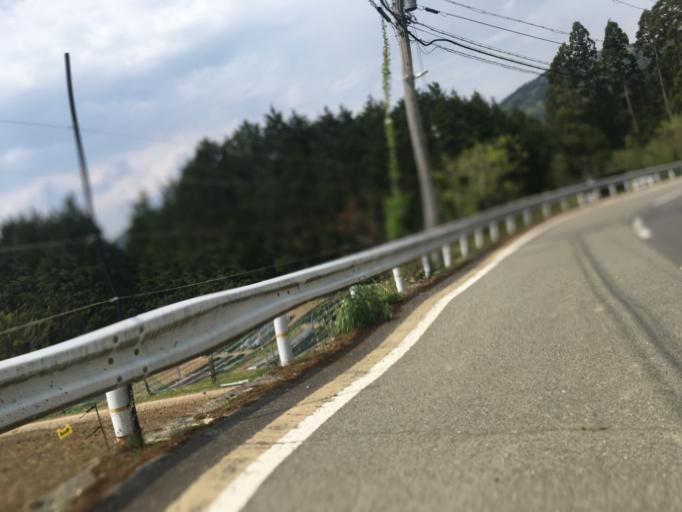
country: JP
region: Kyoto
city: Kameoka
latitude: 35.0811
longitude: 135.6104
